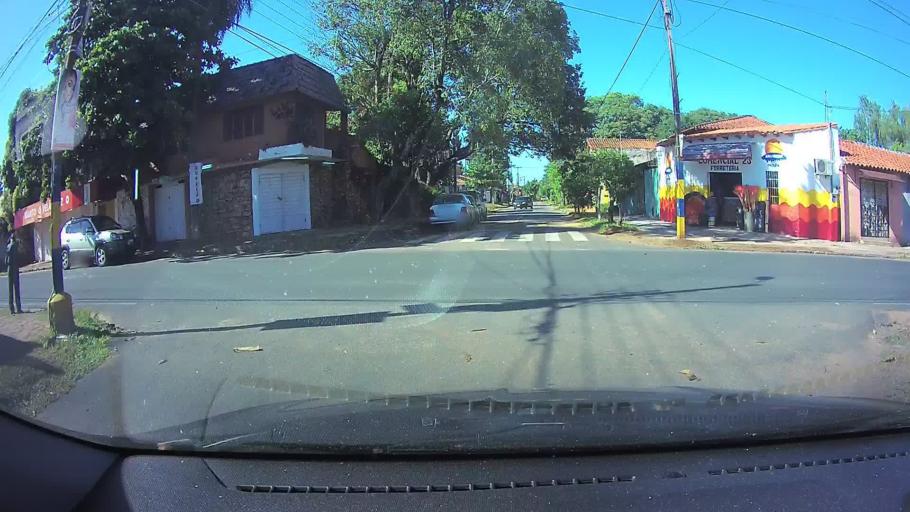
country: PY
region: Central
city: Fernando de la Mora
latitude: -25.2753
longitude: -57.5145
